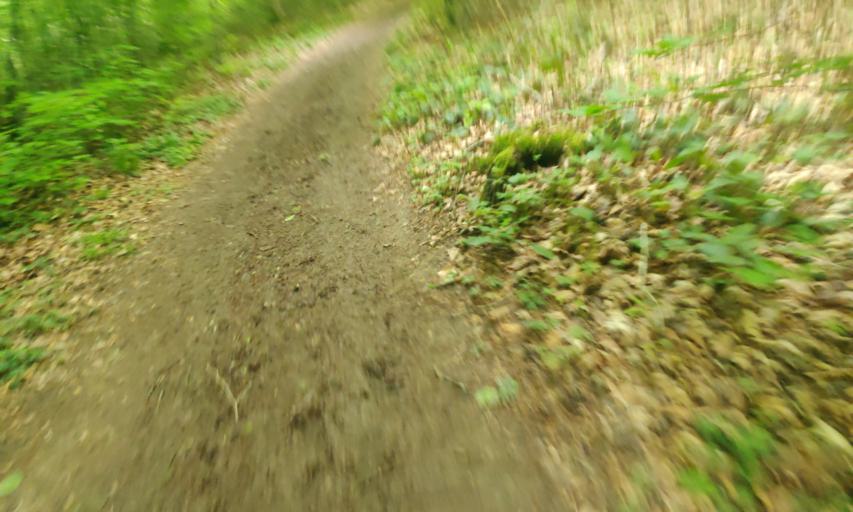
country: CH
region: Fribourg
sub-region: Sarine District
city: Marly
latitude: 46.7874
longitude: 7.1573
